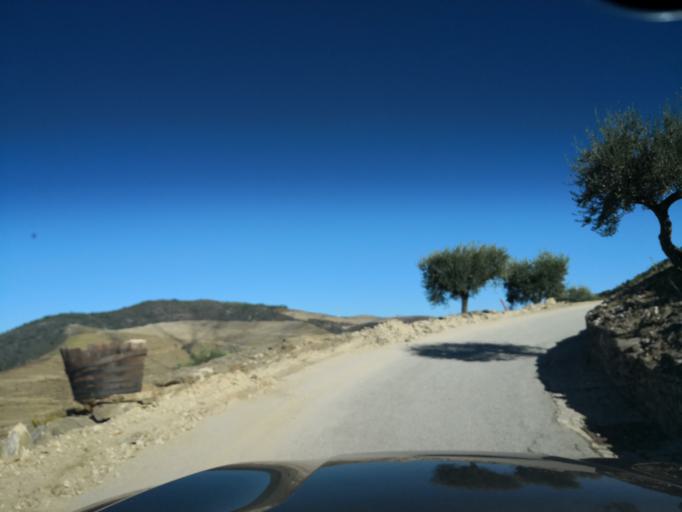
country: PT
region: Viseu
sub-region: Tabuaco
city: Tabuaco
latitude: 41.1741
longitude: -7.5155
